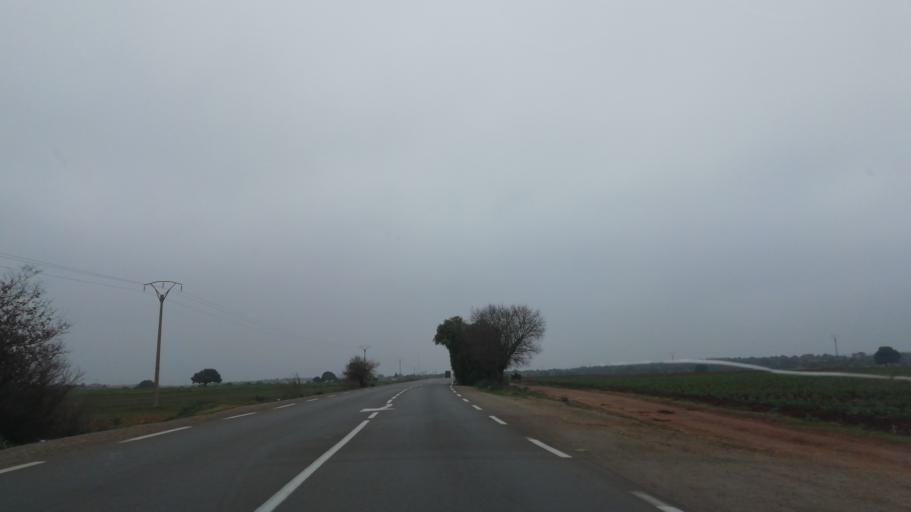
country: DZ
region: Mascara
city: Mascara
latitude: 35.3076
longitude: 0.4191
